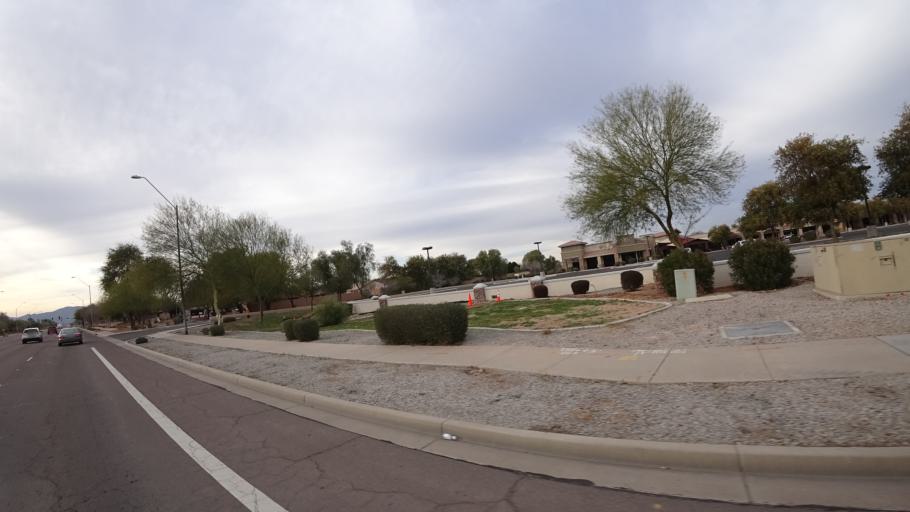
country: US
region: Arizona
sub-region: Maricopa County
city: Surprise
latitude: 33.6242
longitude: -112.3960
